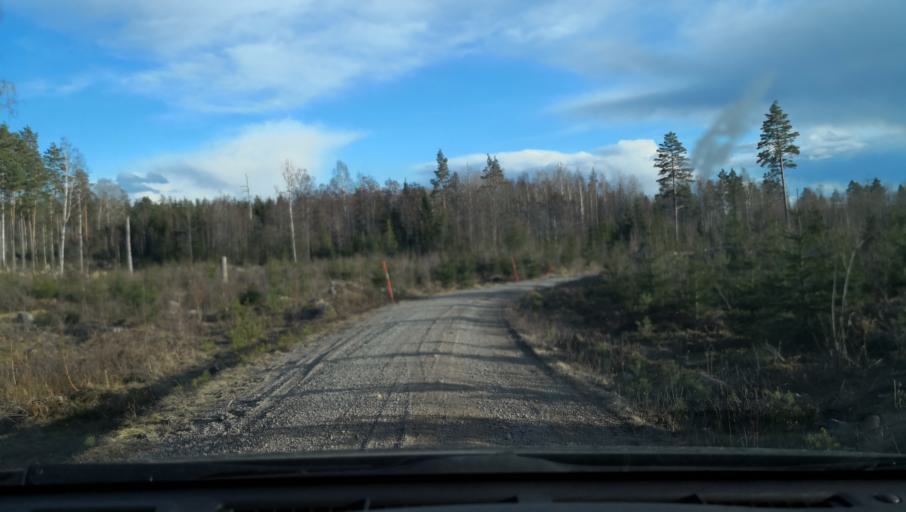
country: SE
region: Vaestmanland
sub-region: Arboga Kommun
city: Arboga
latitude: 59.4325
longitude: 15.7529
